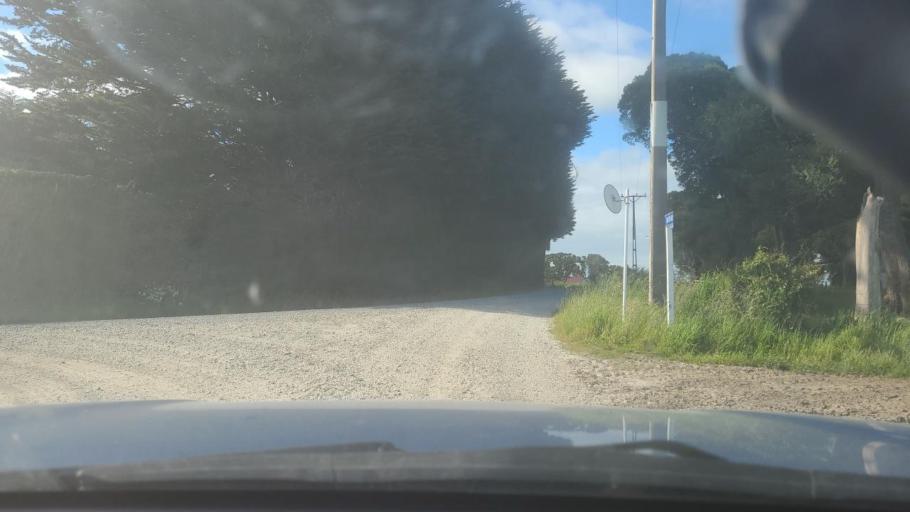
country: NZ
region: Southland
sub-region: Gore District
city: Gore
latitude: -46.4734
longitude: 168.7840
